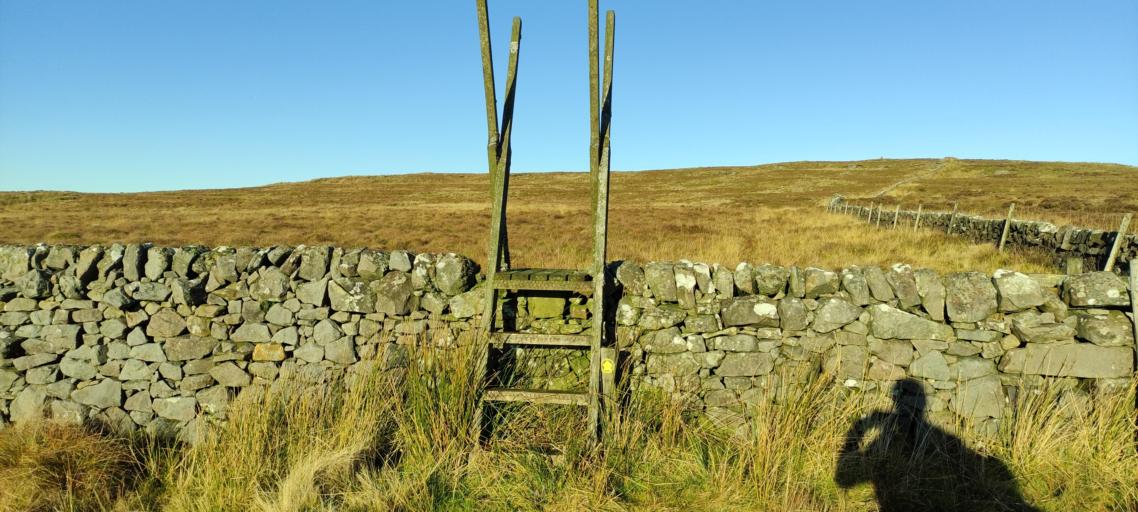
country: GB
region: Scotland
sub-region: Dumfries and Galloway
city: Langholm
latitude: 55.1914
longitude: -2.9558
